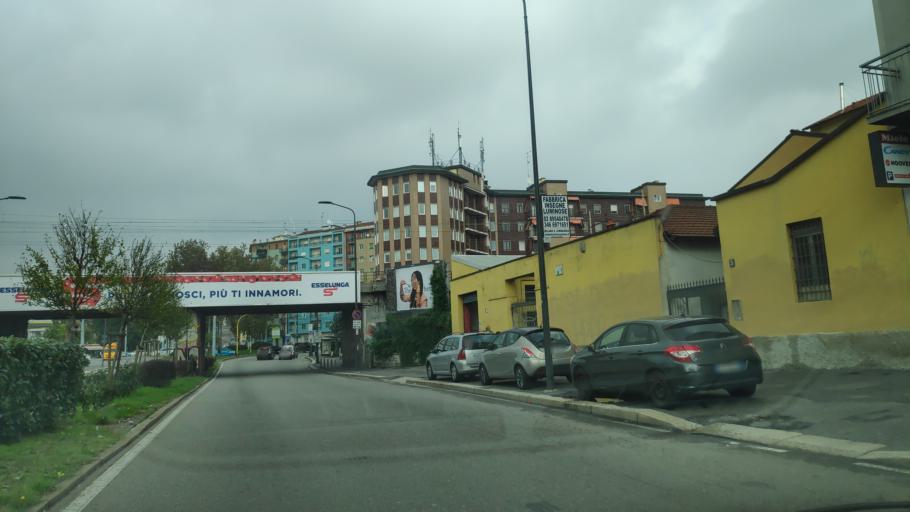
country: IT
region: Lombardy
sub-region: Citta metropolitana di Milano
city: Milano
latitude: 45.4426
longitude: 9.1727
